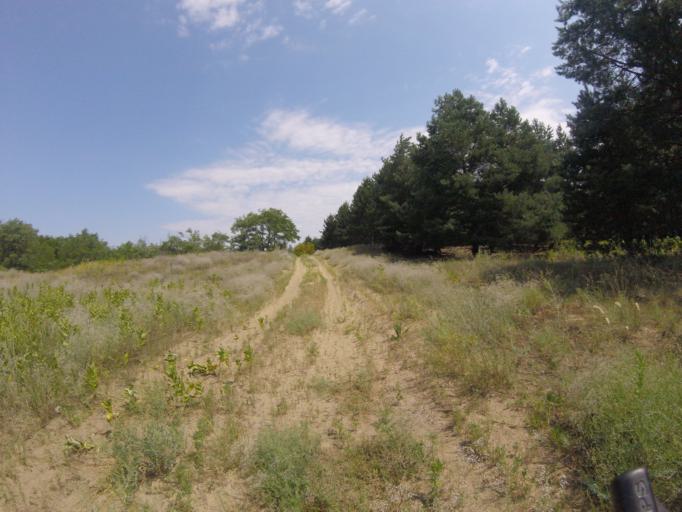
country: HU
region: Bacs-Kiskun
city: Jaszszentlaszlo
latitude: 46.6122
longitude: 19.7225
